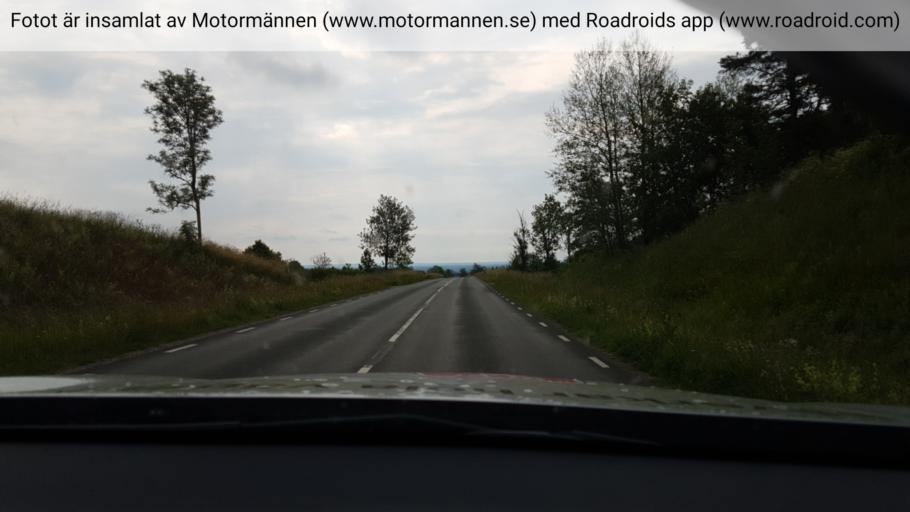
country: SE
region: Vaestra Goetaland
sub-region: Skovde Kommun
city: Skultorp
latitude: 58.3292
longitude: 13.7941
